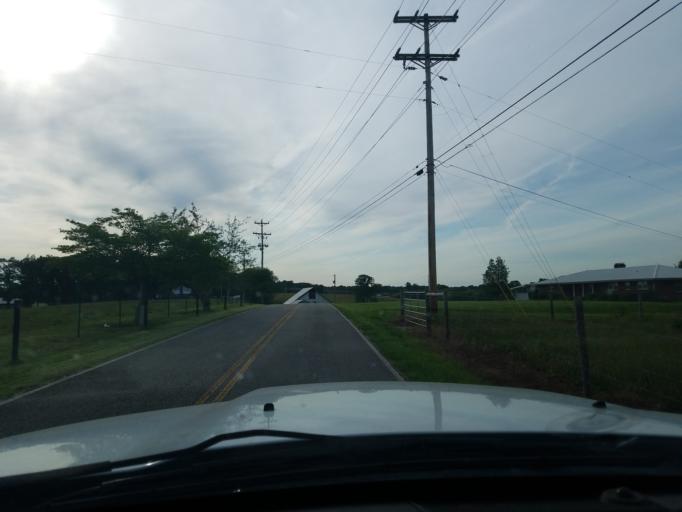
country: US
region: Tennessee
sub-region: Putnam County
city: Baxter
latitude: 36.1317
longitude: -85.5745
